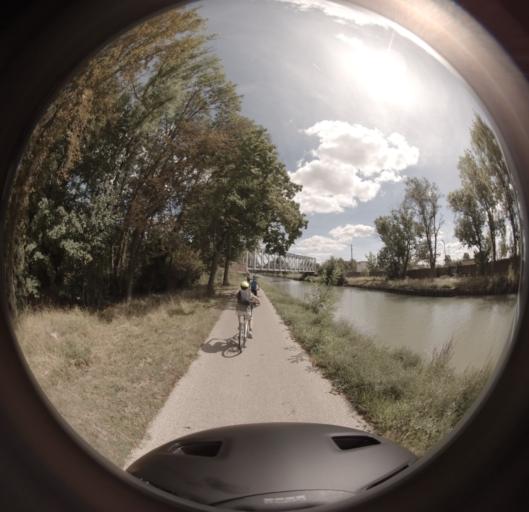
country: FR
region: Midi-Pyrenees
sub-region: Departement du Tarn-et-Garonne
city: Castelsarrasin
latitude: 44.0293
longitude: 1.1433
